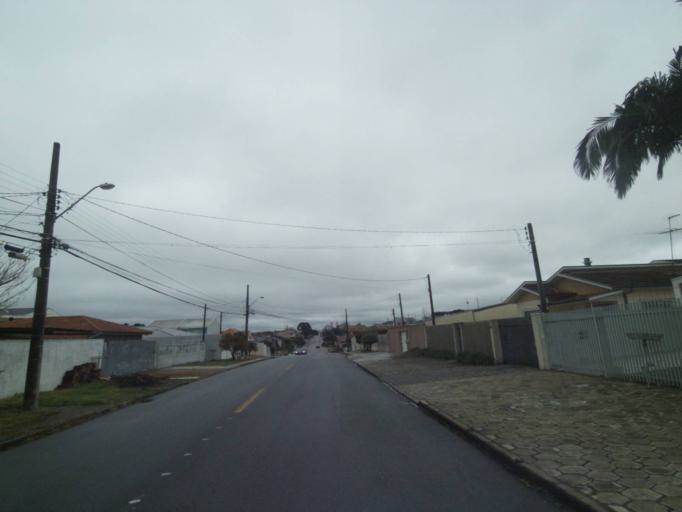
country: BR
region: Parana
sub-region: Curitiba
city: Curitiba
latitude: -25.5033
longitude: -49.3003
